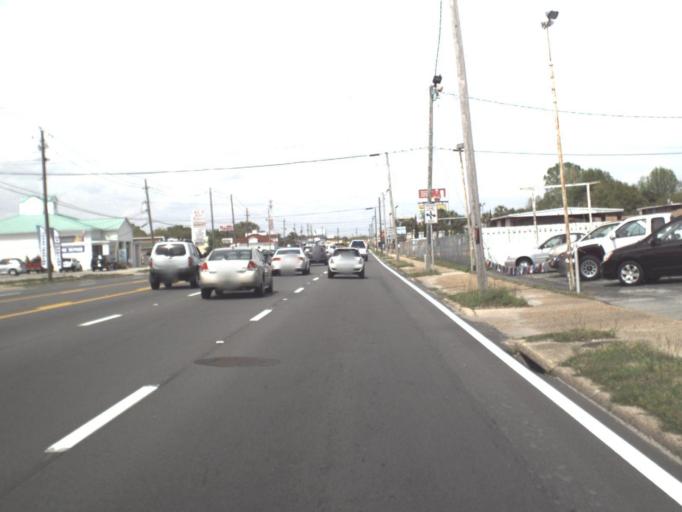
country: US
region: Florida
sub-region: Okaloosa County
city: Ocean City
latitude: 30.4349
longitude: -86.6028
